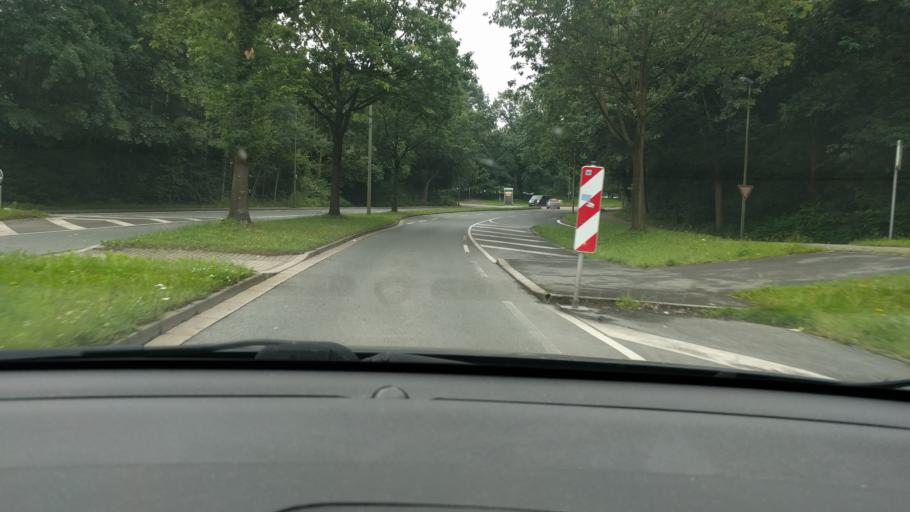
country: DE
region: North Rhine-Westphalia
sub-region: Regierungsbezirk Arnsberg
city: Bochum
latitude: 51.4518
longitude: 7.2735
